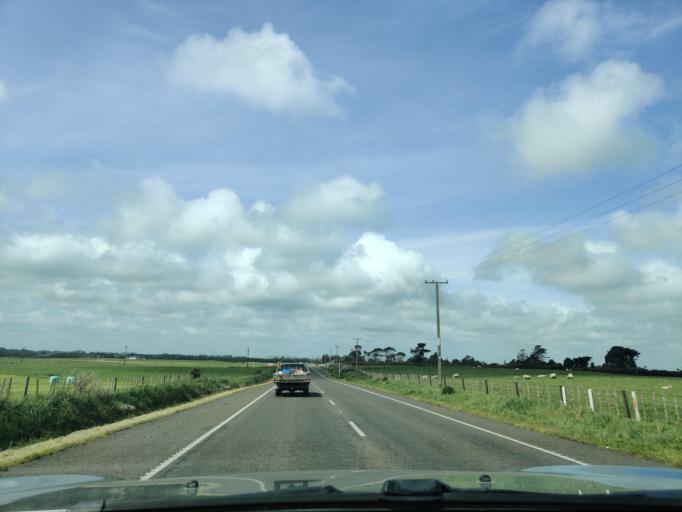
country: NZ
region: Taranaki
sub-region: South Taranaki District
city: Patea
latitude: -39.7678
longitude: 174.6028
